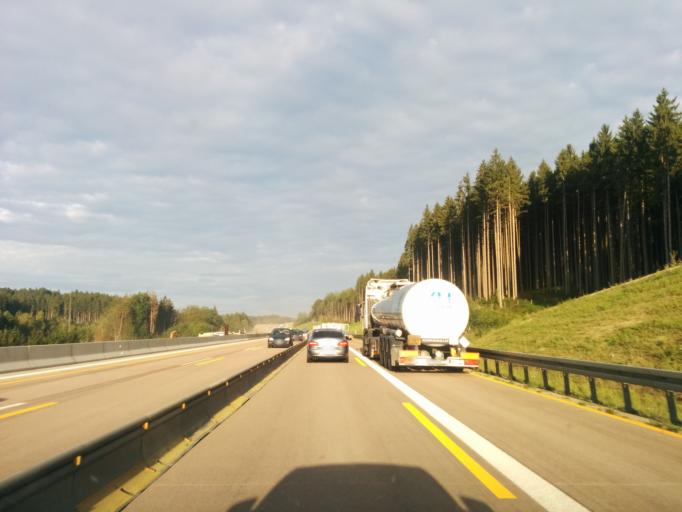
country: DE
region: Bavaria
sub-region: Swabia
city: Aystetten
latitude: 48.4201
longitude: 10.7844
